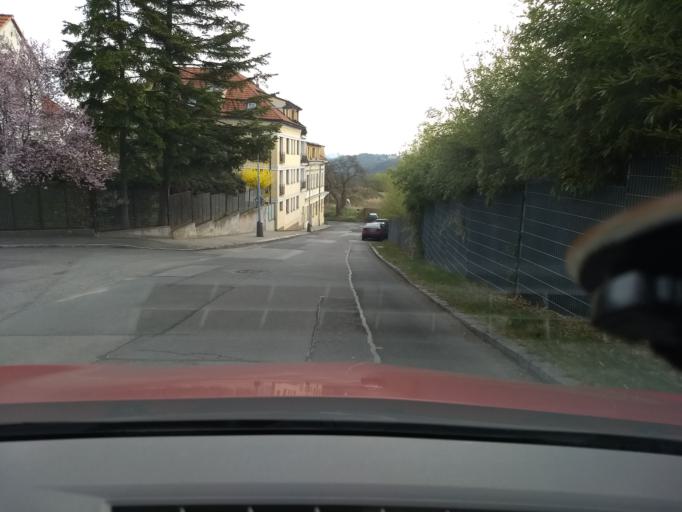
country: CZ
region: Central Bohemia
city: Horomerice
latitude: 50.1005
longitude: 14.3490
